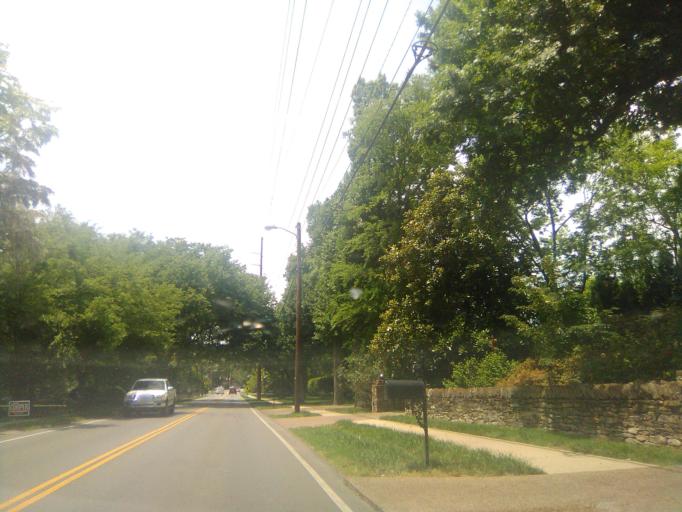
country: US
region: Tennessee
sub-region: Davidson County
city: Belle Meade
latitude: 36.0946
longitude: -86.8542
